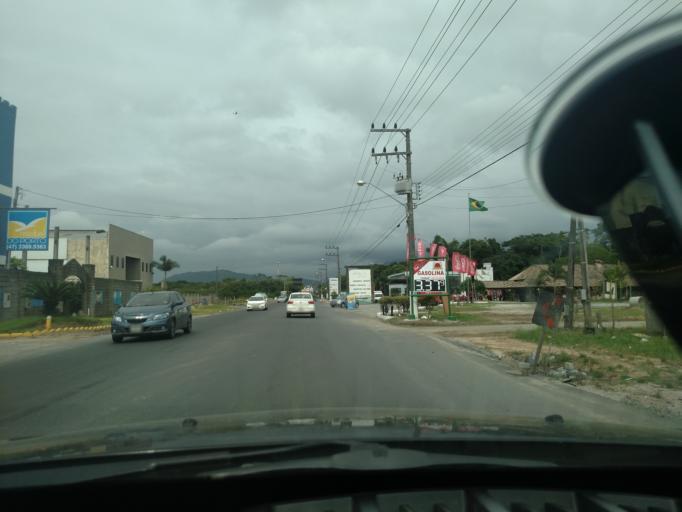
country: BR
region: Santa Catarina
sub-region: Porto Belo
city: Porto Belo
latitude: -27.1591
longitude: -48.5984
